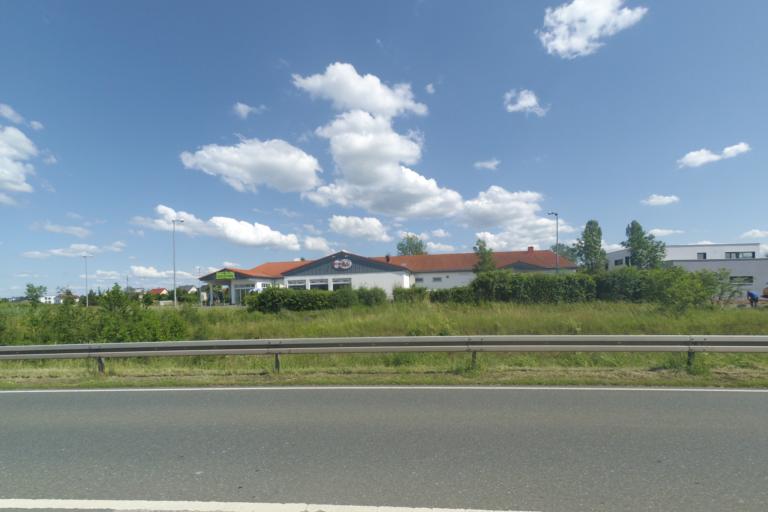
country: DE
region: Bavaria
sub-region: Regierungsbezirk Mittelfranken
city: Adelsdorf
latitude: 49.7092
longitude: 10.8829
